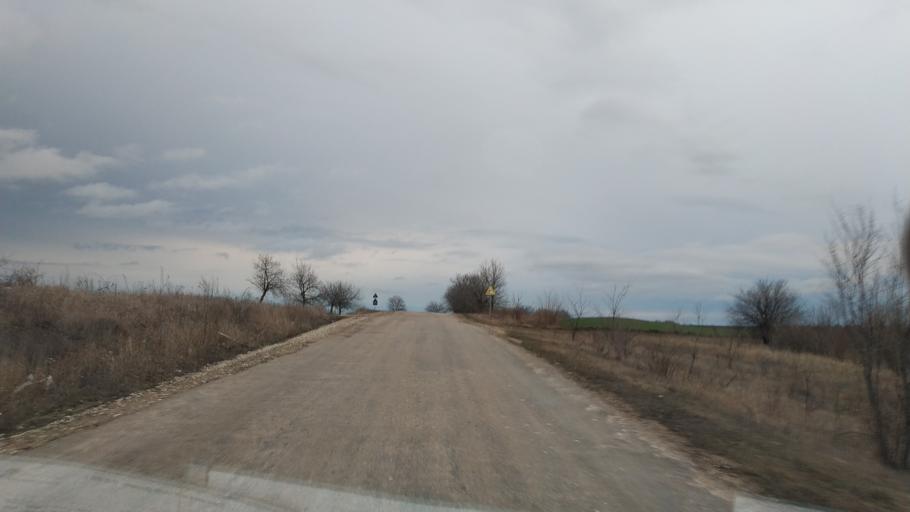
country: MD
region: Causeni
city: Causeni
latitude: 46.6107
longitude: 29.4012
